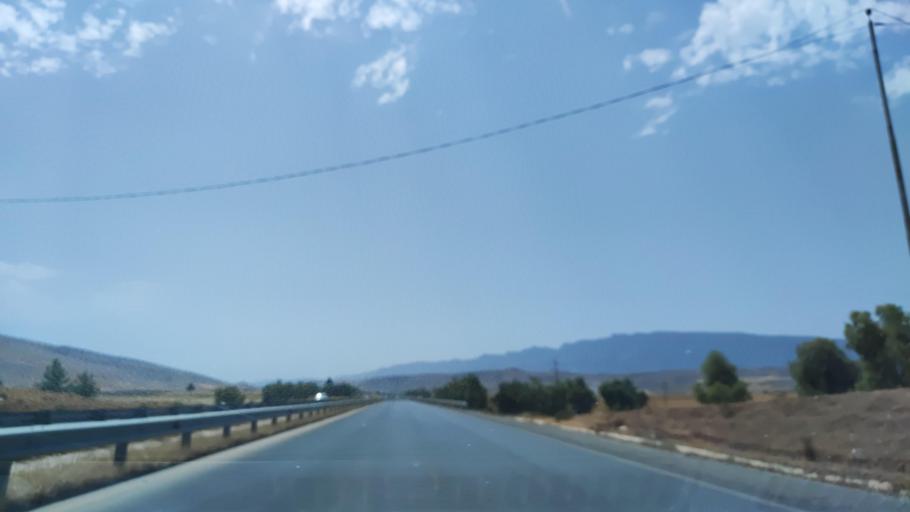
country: IQ
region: Arbil
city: Shaqlawah
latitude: 36.4756
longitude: 44.3807
